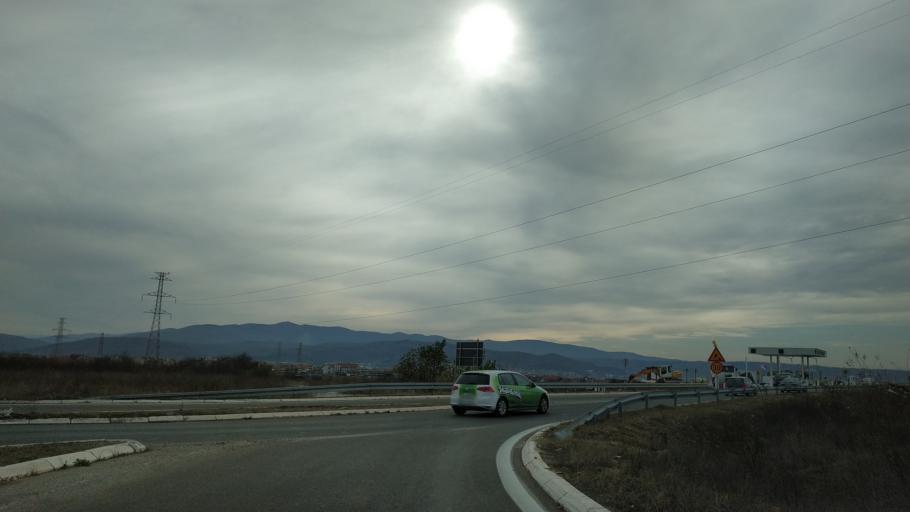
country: RS
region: Central Serbia
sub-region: Nisavski Okrug
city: Nis
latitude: 43.3433
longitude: 21.9372
